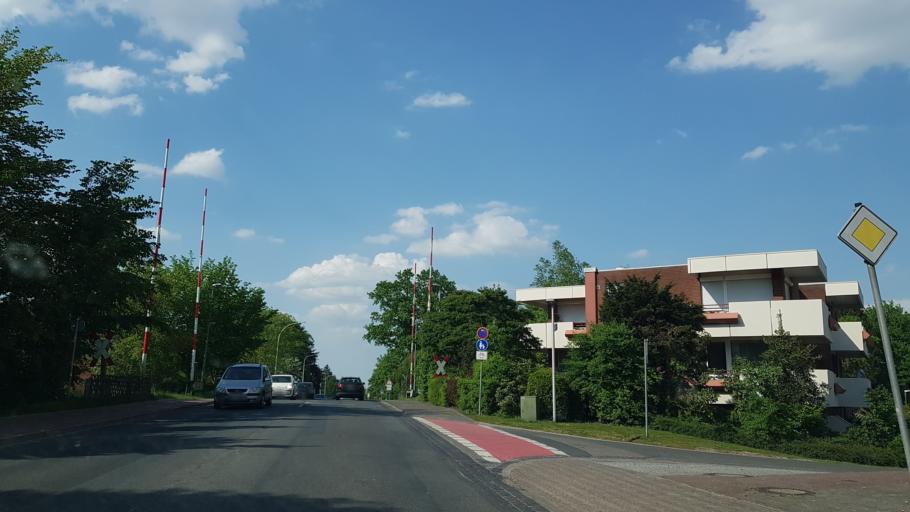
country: DE
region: Lower Saxony
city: Langen
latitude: 53.6000
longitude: 8.5955
